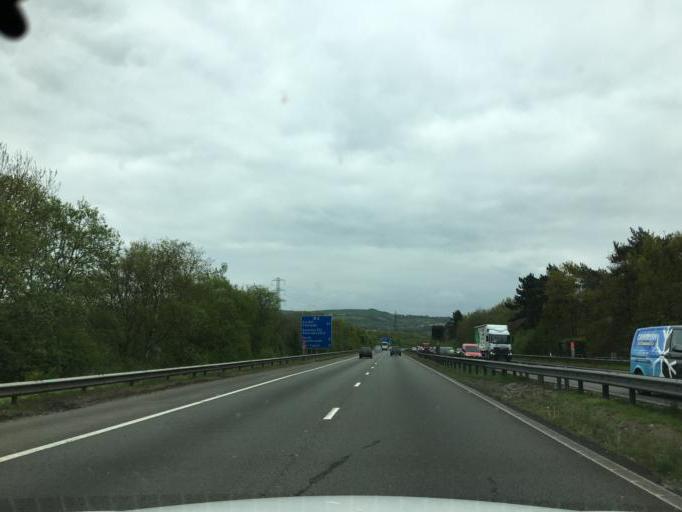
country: GB
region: Wales
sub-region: City and County of Swansea
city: Clydach
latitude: 51.6763
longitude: -3.9035
